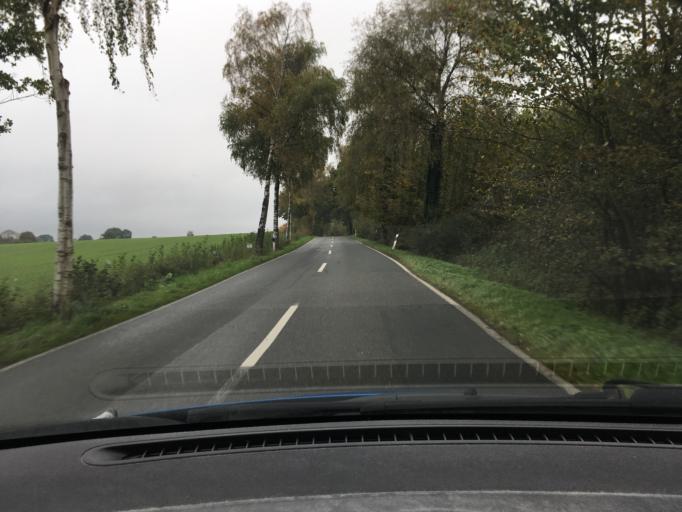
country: DE
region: Schleswig-Holstein
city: Bosau
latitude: 54.0956
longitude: 10.4631
